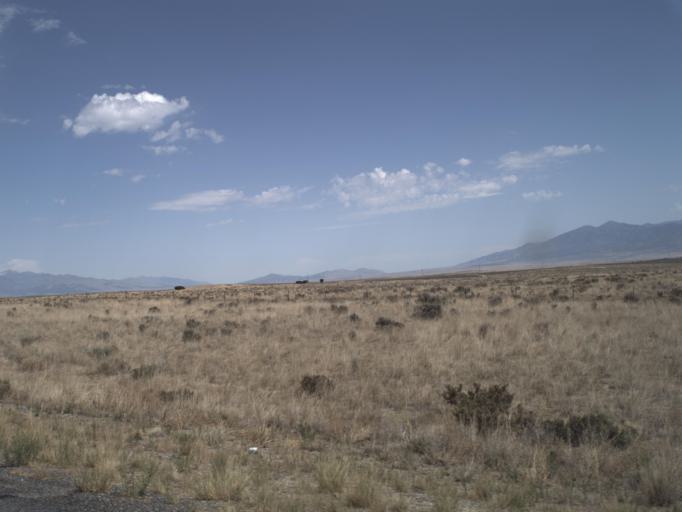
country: US
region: Utah
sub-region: Utah County
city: Eagle Mountain
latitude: 40.0576
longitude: -112.3067
